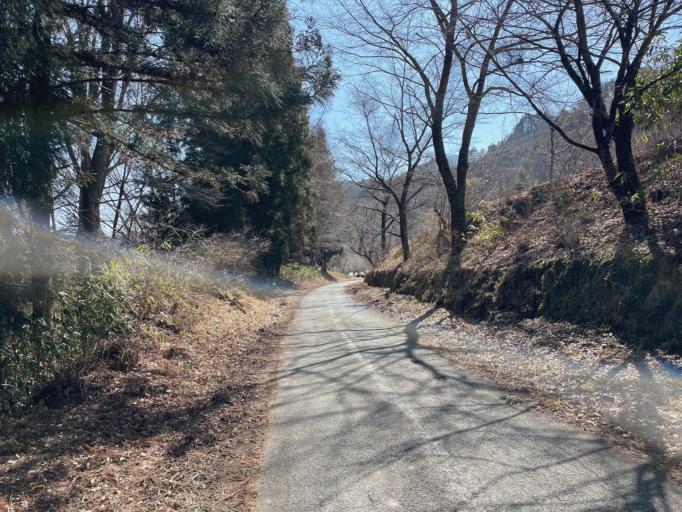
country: JP
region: Gunma
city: Nakanojomachi
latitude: 36.5752
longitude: 138.6251
